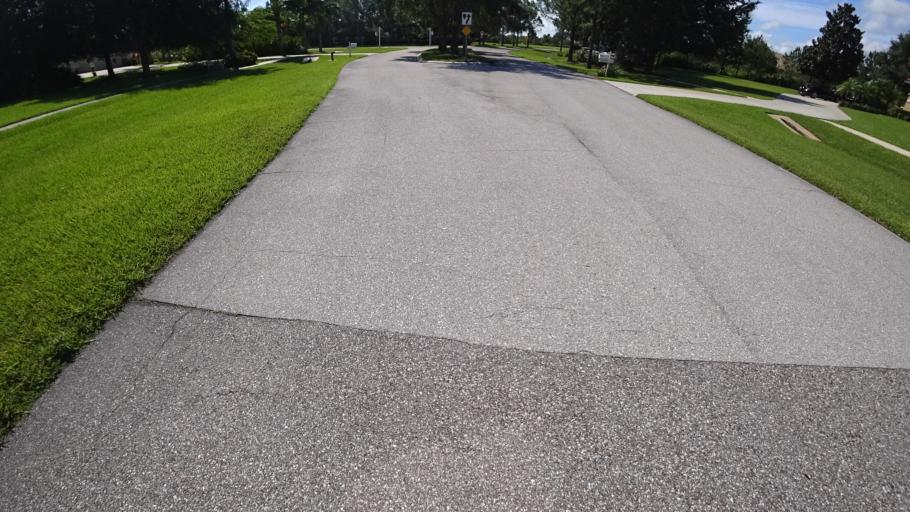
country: US
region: Florida
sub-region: Sarasota County
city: Fruitville
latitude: 27.3942
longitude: -82.3163
